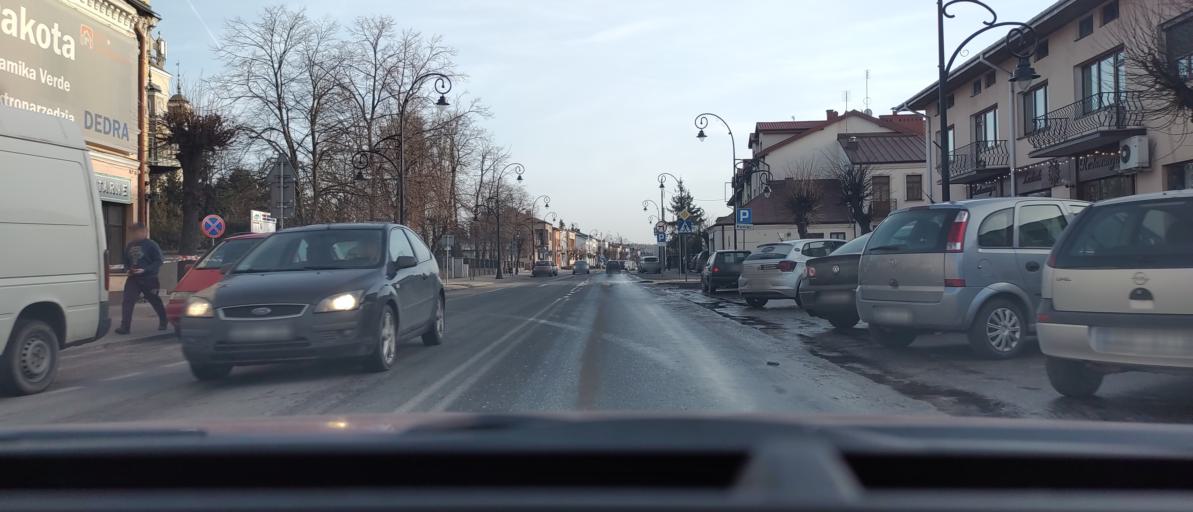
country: PL
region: Masovian Voivodeship
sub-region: Powiat bialobrzeski
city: Bialobrzegi
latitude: 51.6515
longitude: 20.9528
